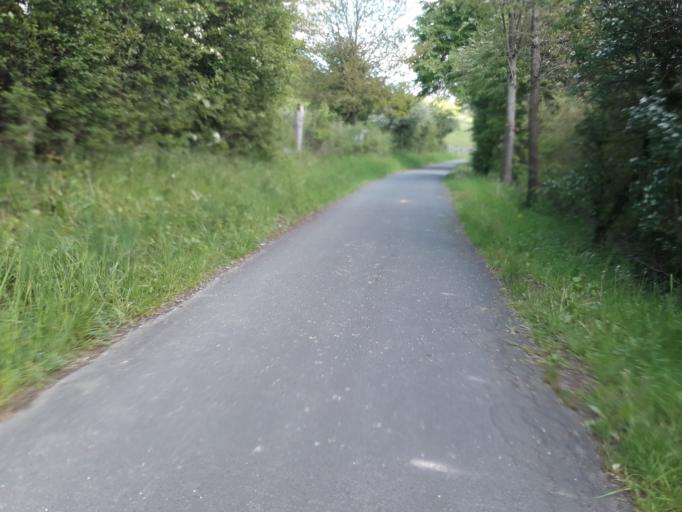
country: DE
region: North Rhine-Westphalia
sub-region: Regierungsbezirk Detmold
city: Paderborn
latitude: 51.6973
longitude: 8.8128
